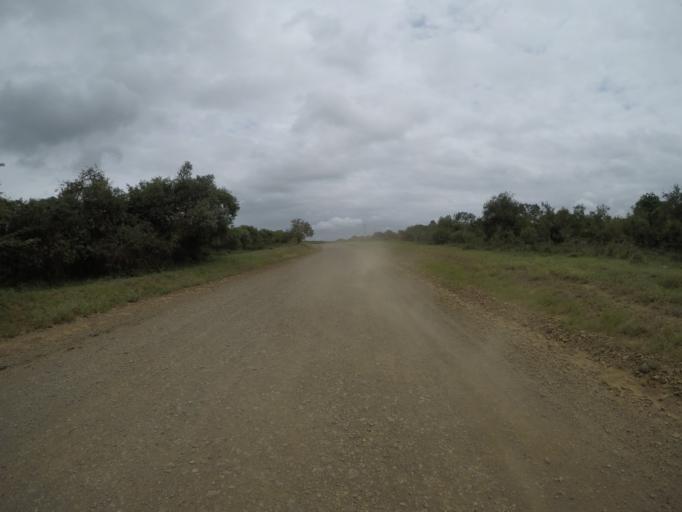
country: ZA
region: KwaZulu-Natal
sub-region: uThungulu District Municipality
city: Empangeni
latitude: -28.5989
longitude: 31.8289
